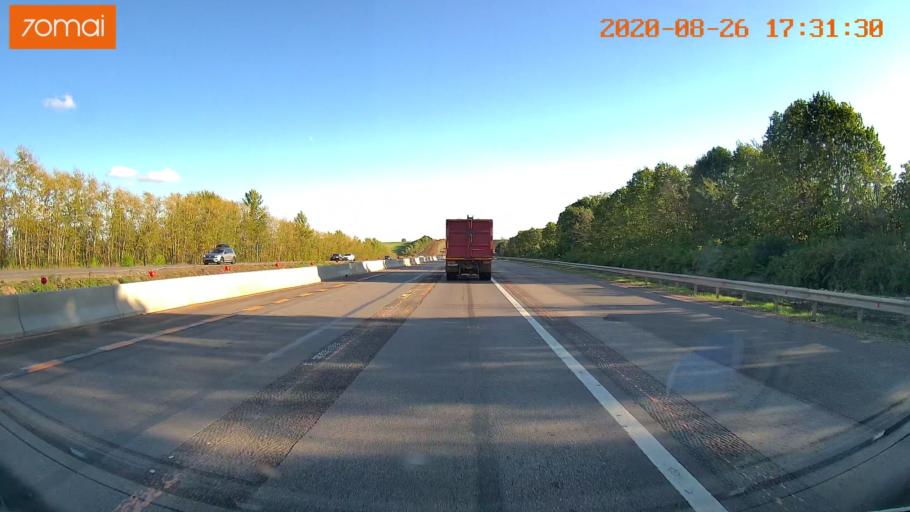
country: RU
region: Tula
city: Kazachka
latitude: 53.4331
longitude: 38.1794
